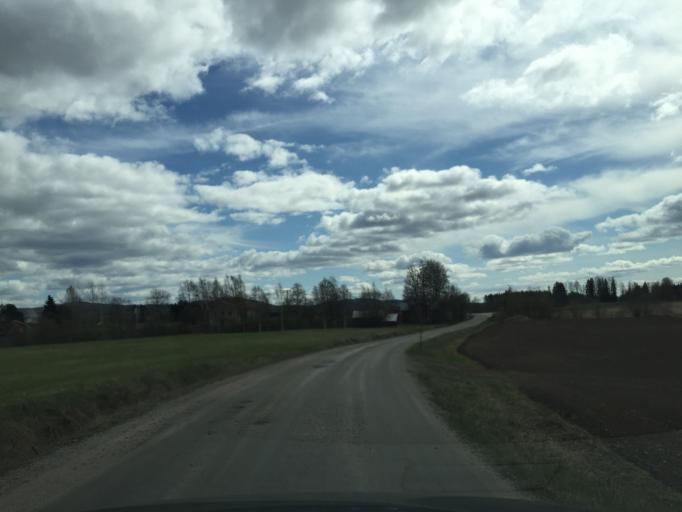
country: SE
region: Gaevleborg
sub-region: Bollnas Kommun
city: Arbra
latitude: 61.5142
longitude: 16.3572
